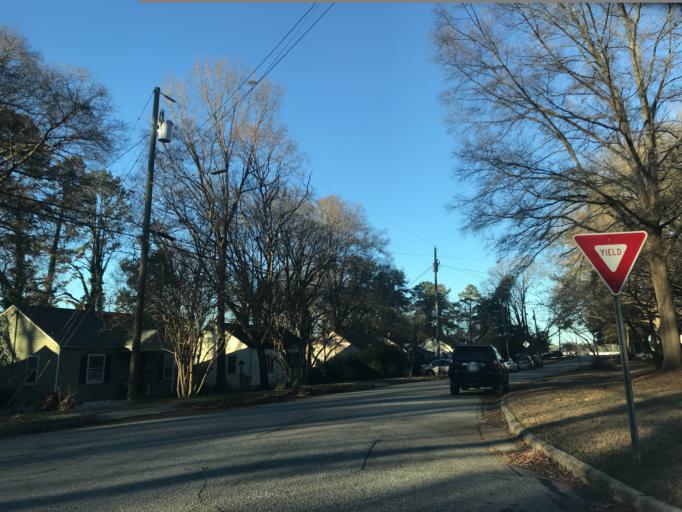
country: US
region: North Carolina
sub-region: Wake County
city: Raleigh
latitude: 35.7989
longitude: -78.6230
